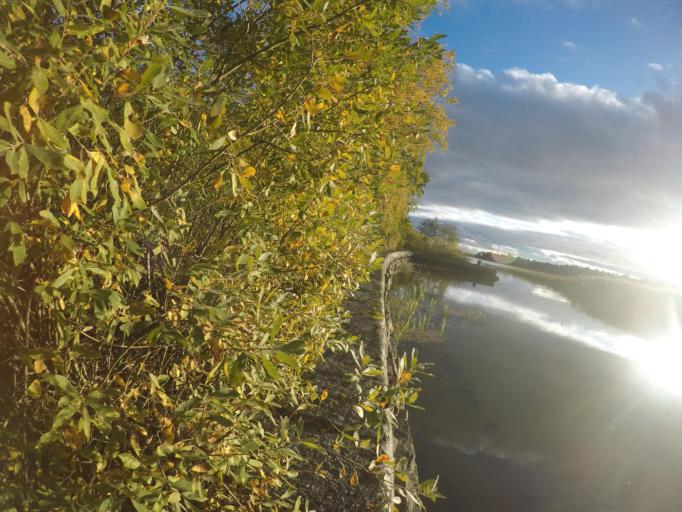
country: SE
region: Vaestmanland
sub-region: Arboga Kommun
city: Tyringe
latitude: 59.2913
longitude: 16.0031
